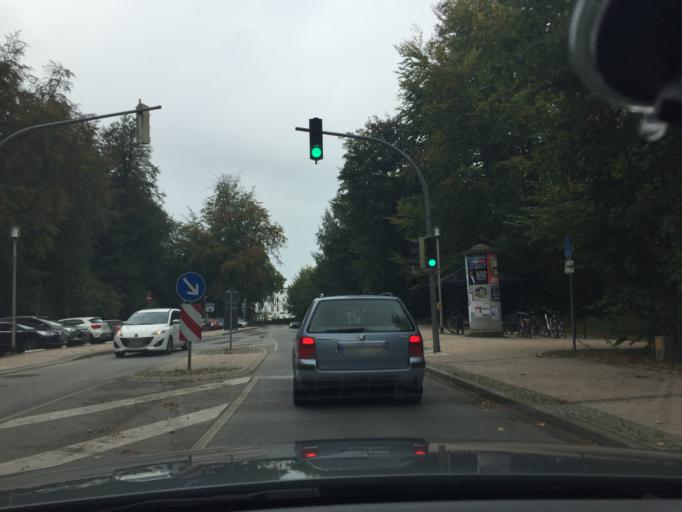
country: DE
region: Mecklenburg-Vorpommern
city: Bad Doberan
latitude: 54.1422
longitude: 11.8446
